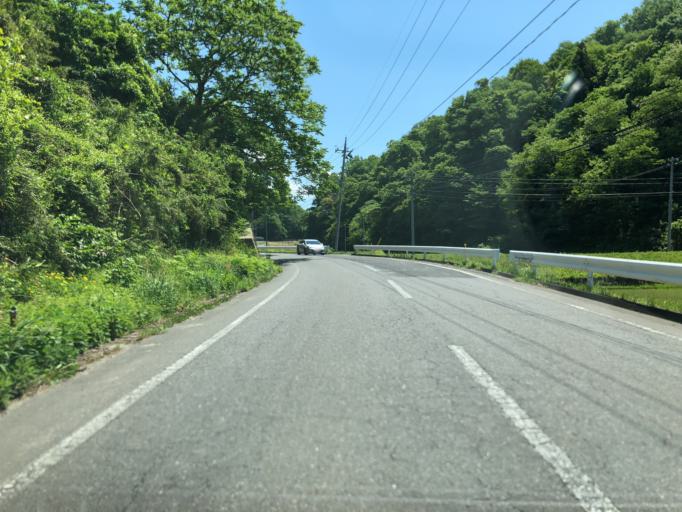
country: JP
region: Fukushima
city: Funehikimachi-funehiki
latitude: 37.4864
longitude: 140.5538
